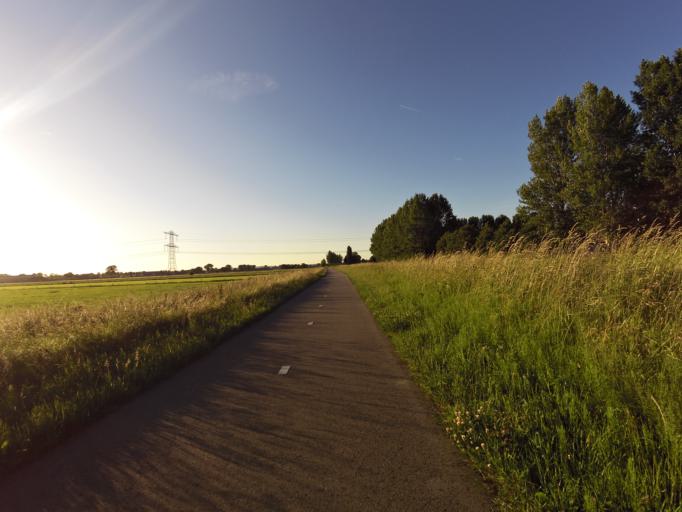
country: NL
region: Gelderland
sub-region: Gemeente Zevenaar
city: Zevenaar
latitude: 51.9527
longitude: 6.0835
